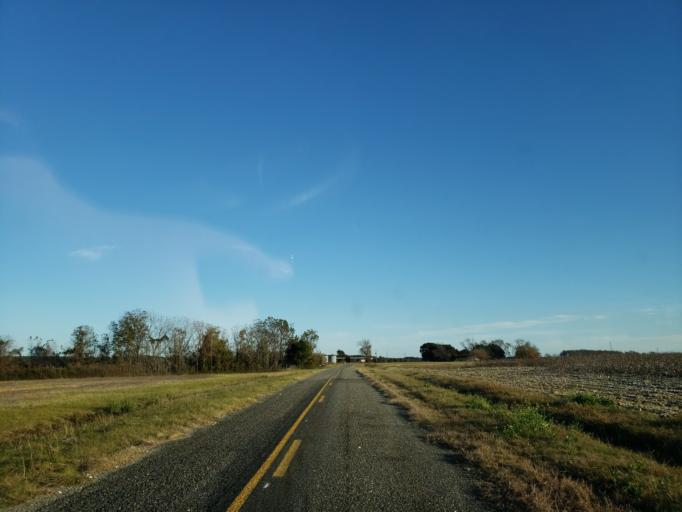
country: US
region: Georgia
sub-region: Dooly County
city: Unadilla
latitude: 32.1984
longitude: -83.7898
